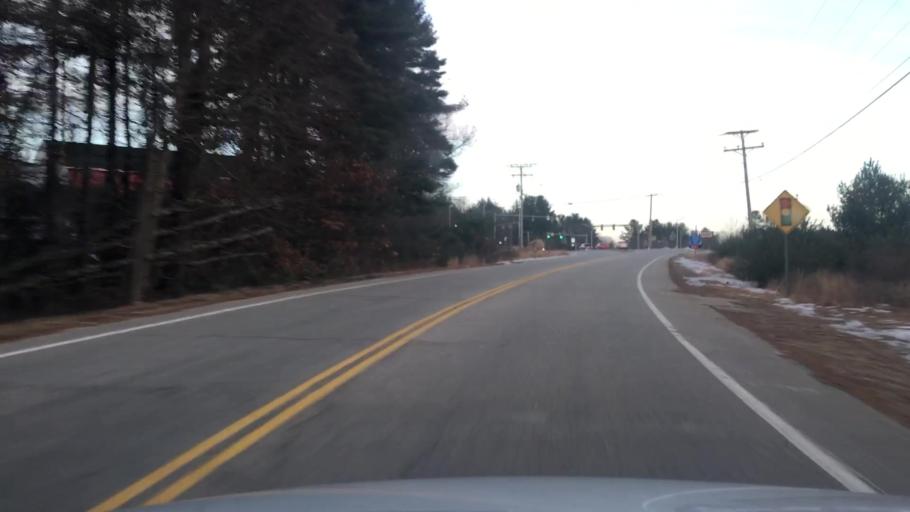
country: US
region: New Hampshire
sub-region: Strafford County
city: Somersworth
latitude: 43.2655
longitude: -70.9090
